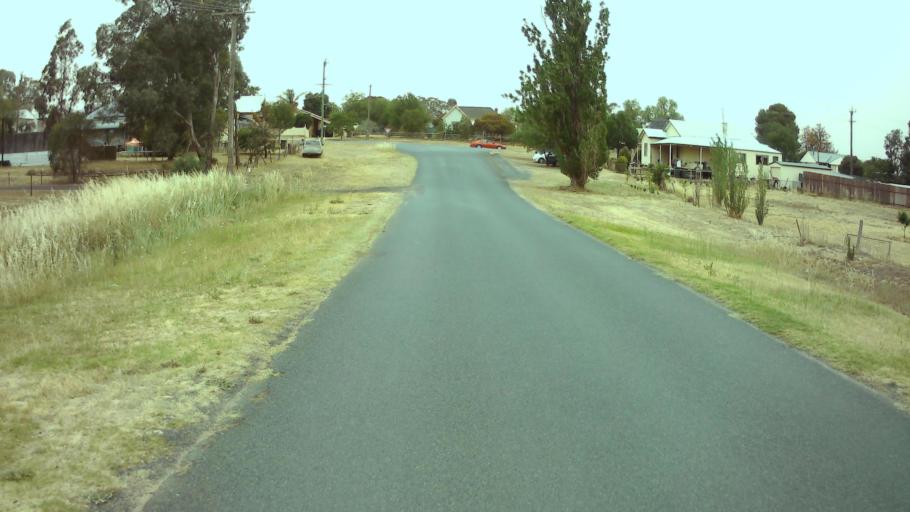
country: AU
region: New South Wales
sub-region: Weddin
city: Grenfell
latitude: -33.8996
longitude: 148.1568
